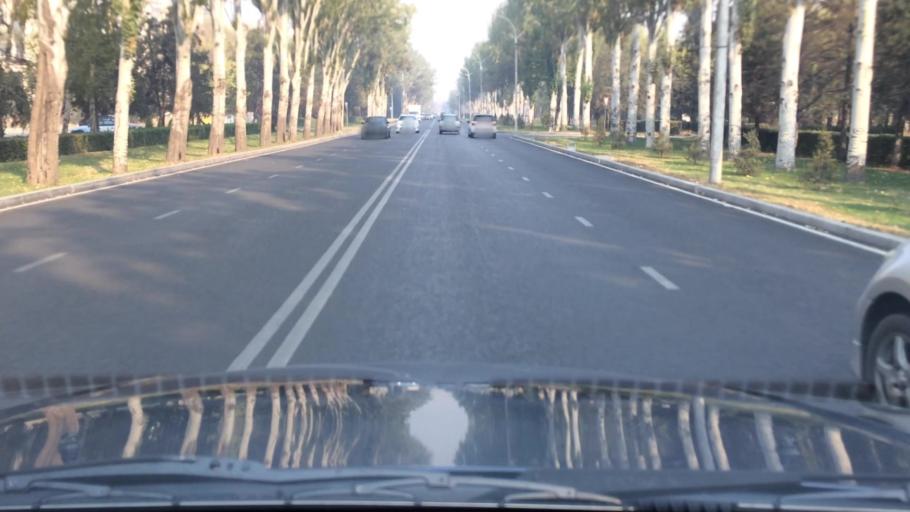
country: KG
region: Chuy
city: Bishkek
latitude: 42.8357
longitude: 74.5856
